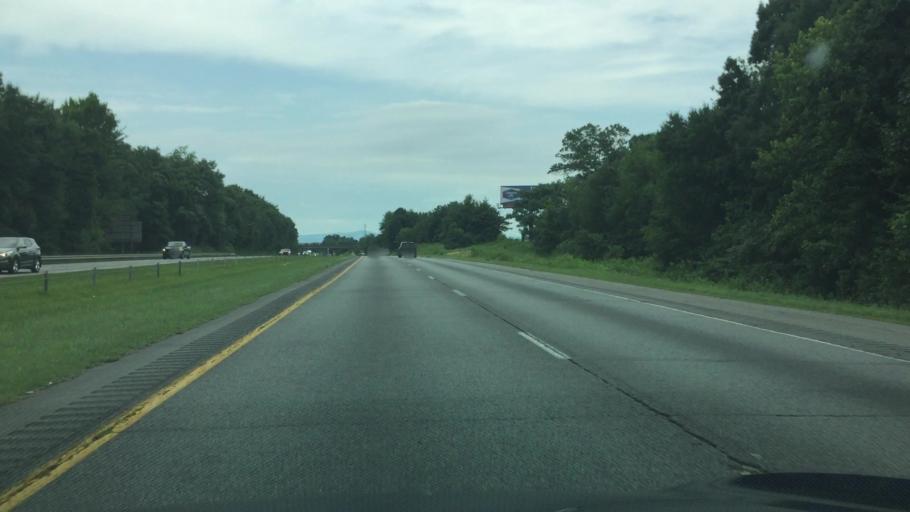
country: US
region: North Carolina
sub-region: Yadkin County
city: Jonesville
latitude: 36.2099
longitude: -80.8107
